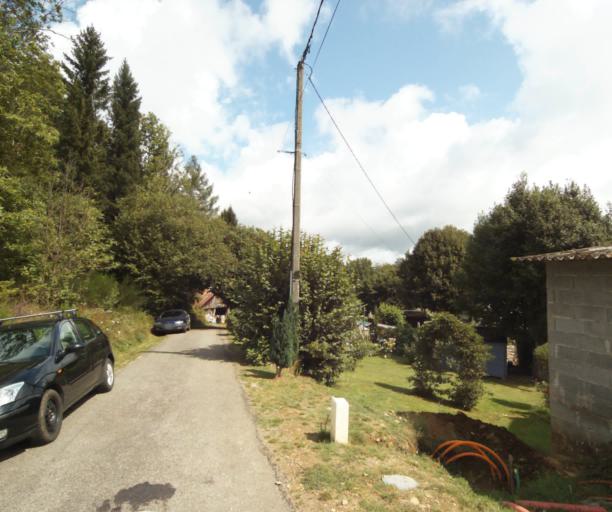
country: FR
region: Limousin
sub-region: Departement de la Correze
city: Sainte-Fortunade
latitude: 45.2025
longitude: 1.8026
